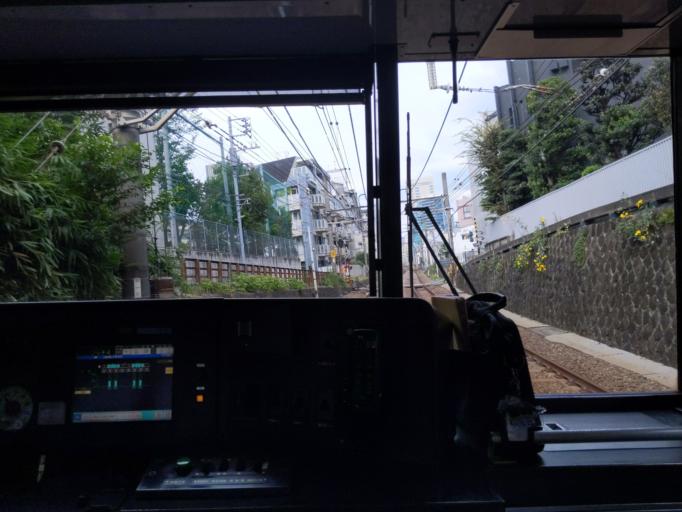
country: JP
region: Tokyo
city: Tokyo
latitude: 35.6806
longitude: 139.6949
